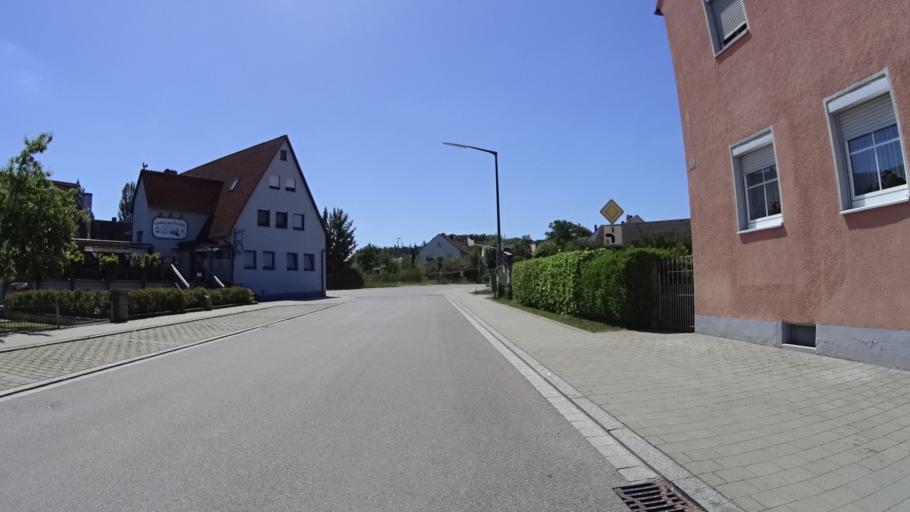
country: DE
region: Bavaria
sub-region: Regierungsbezirk Mittelfranken
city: Pfofeld
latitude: 49.1195
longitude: 10.8587
